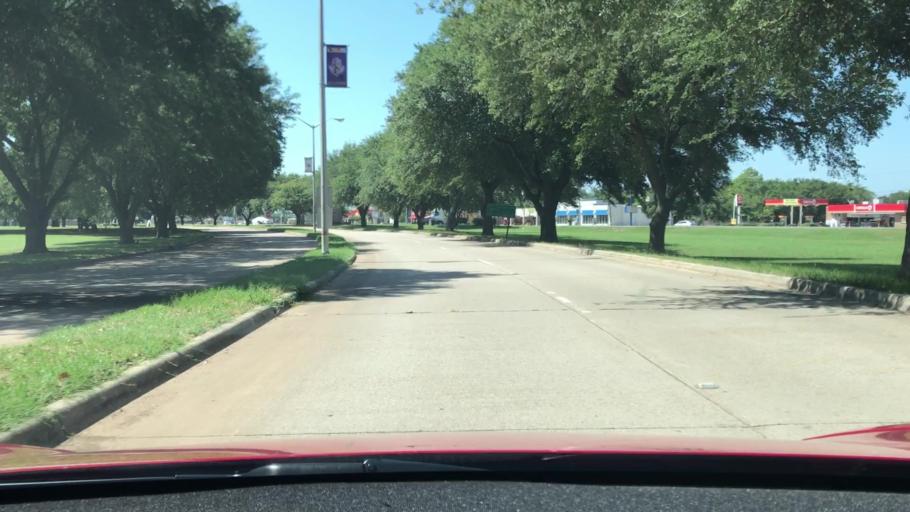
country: US
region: Louisiana
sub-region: Bossier Parish
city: Bossier City
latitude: 32.4281
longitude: -93.7086
